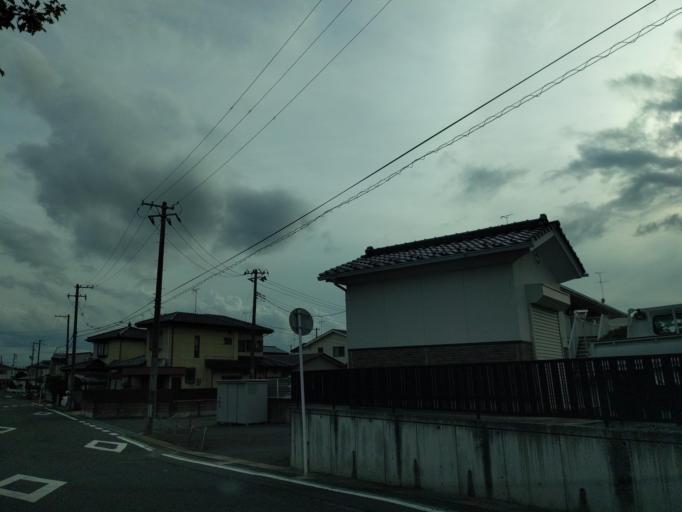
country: JP
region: Fukushima
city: Koriyama
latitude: 37.4049
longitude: 140.3309
